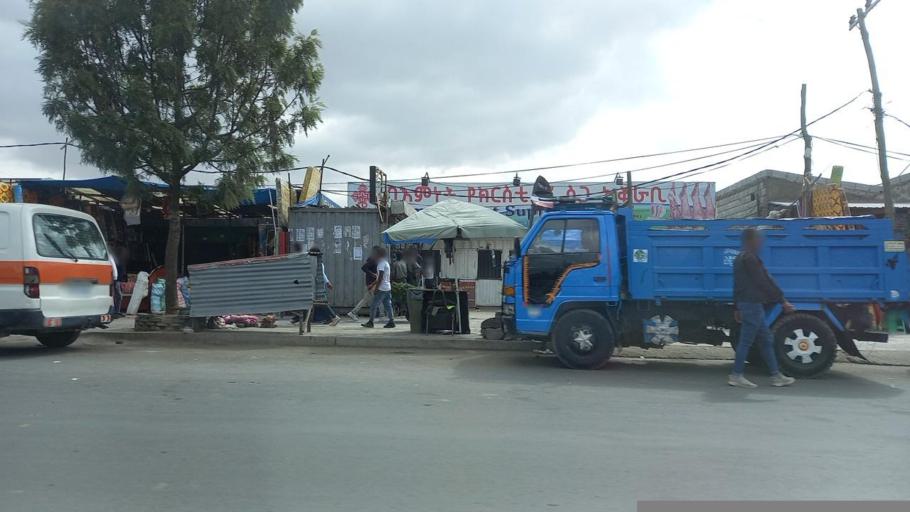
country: ET
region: Adis Abeba
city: Addis Ababa
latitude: 9.0205
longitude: 38.8608
